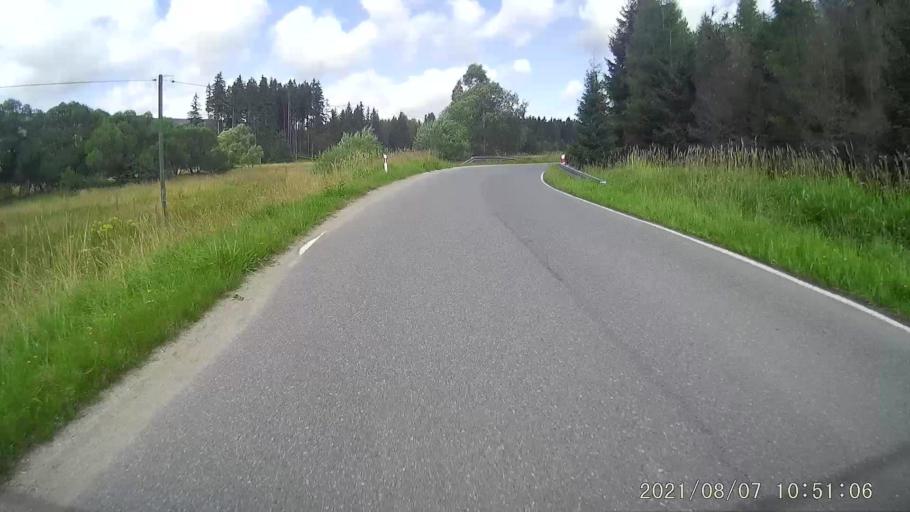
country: PL
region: Lower Silesian Voivodeship
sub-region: Powiat klodzki
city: Polanica-Zdroj
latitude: 50.2916
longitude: 16.4677
